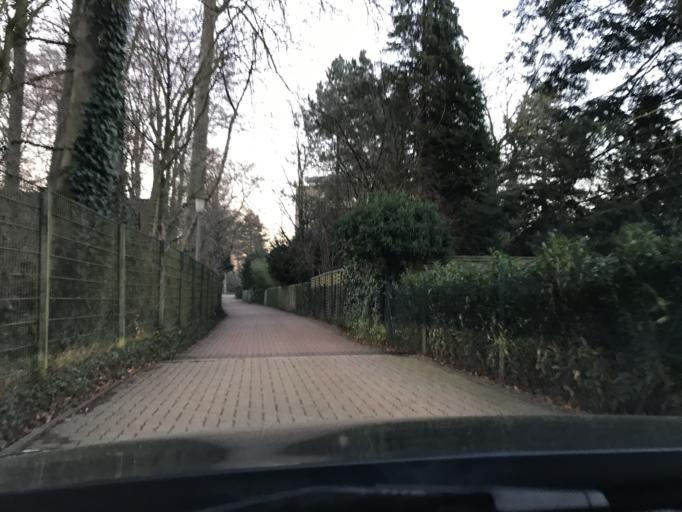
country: DE
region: North Rhine-Westphalia
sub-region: Regierungsbezirk Dusseldorf
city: Krefeld
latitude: 51.3409
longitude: 6.6053
